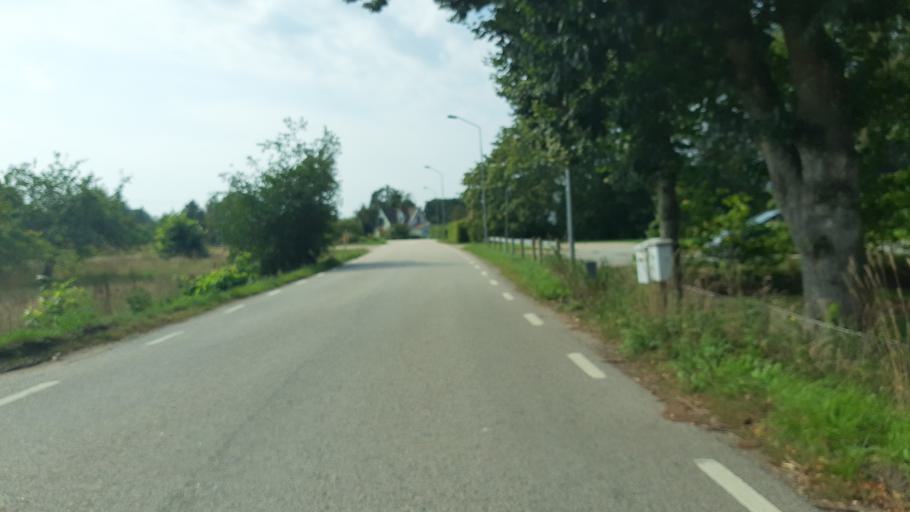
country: SE
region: Blekinge
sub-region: Karlskrona Kommun
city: Nattraby
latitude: 56.2271
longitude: 15.4204
